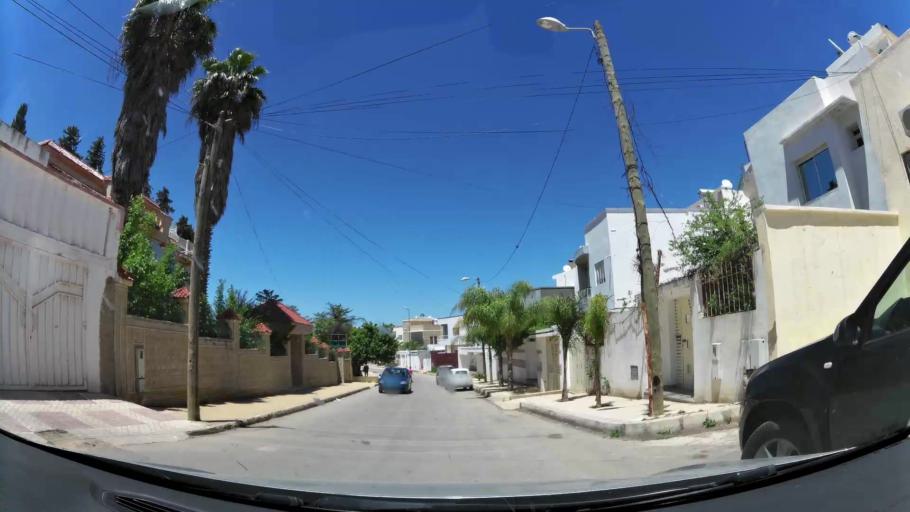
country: MA
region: Meknes-Tafilalet
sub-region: Meknes
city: Meknes
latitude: 33.9044
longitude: -5.5577
